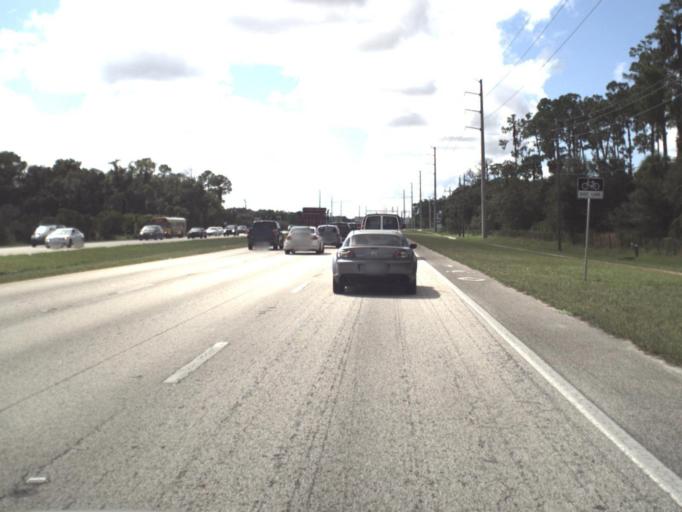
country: US
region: Florida
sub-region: Manatee County
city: Samoset
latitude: 27.4462
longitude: -82.4770
